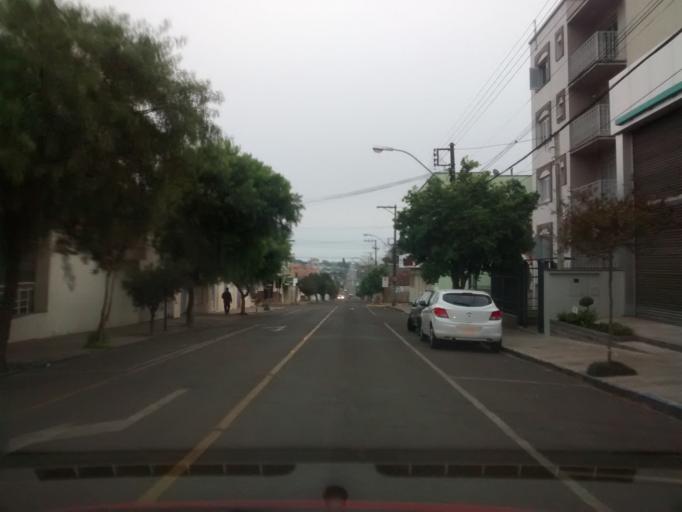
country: BR
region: Rio Grande do Sul
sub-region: Vacaria
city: Vacaria
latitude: -28.5022
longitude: -50.9381
